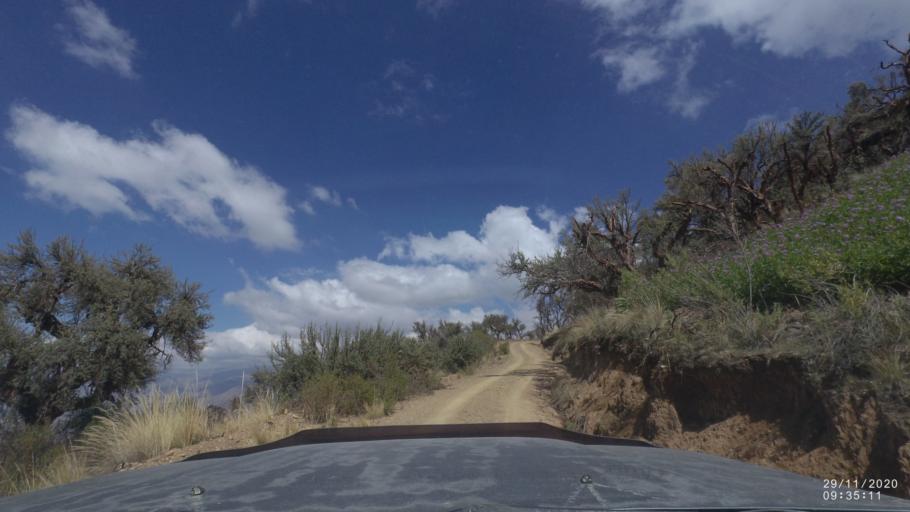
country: BO
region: Cochabamba
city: Cochabamba
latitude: -17.3109
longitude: -66.1887
